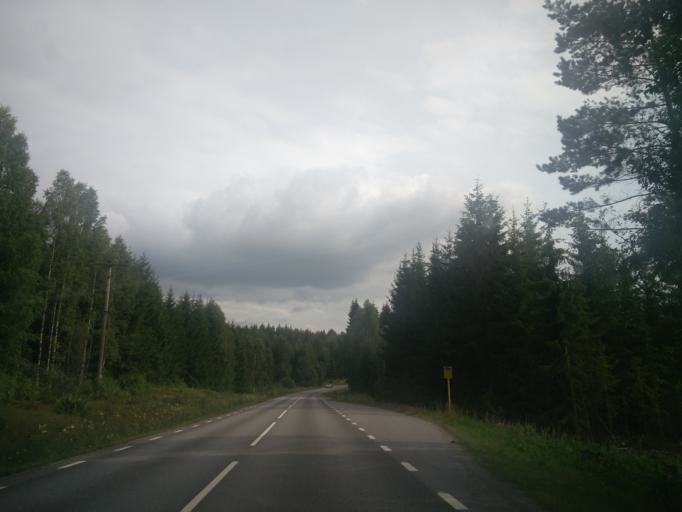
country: SE
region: Vaermland
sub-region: Arvika Kommun
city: Arvika
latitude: 59.7313
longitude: 12.5634
